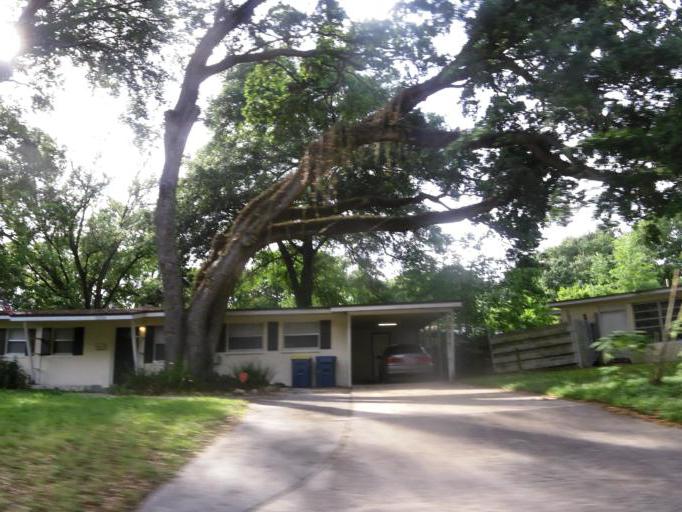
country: US
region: Florida
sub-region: Duval County
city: Jacksonville
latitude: 30.3345
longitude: -81.5879
